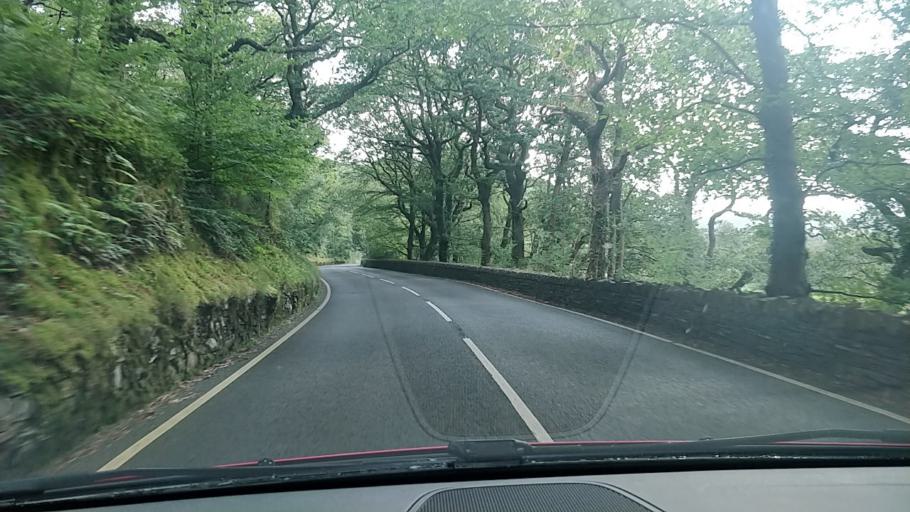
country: GB
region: Wales
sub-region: Gwynedd
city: Maentwrog
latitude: 52.9398
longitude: -3.9987
